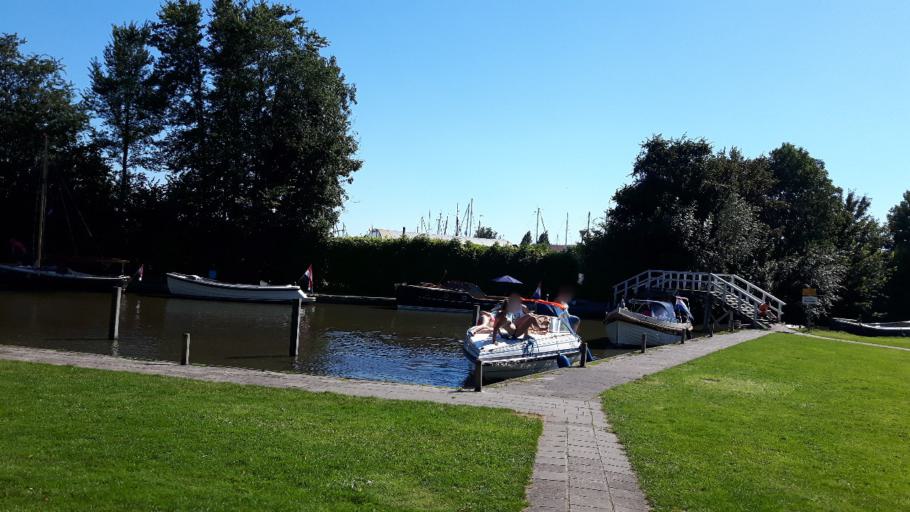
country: NL
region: Friesland
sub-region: Sudwest Fryslan
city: Woudsend
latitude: 52.8935
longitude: 5.6452
